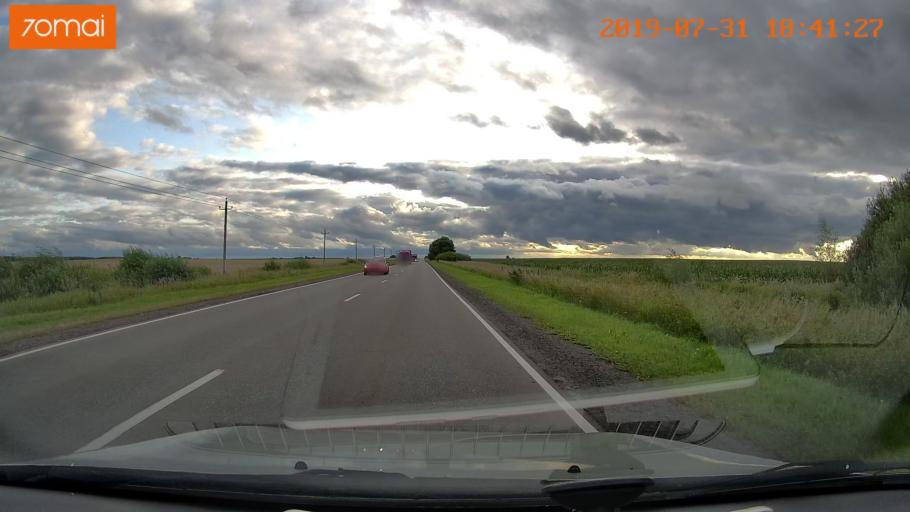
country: RU
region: Moskovskaya
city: Voskresensk
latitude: 55.2555
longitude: 38.6127
